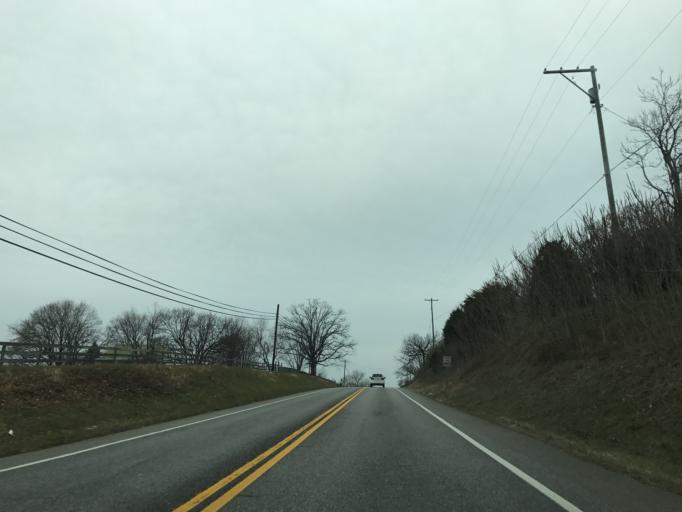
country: US
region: Maryland
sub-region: Frederick County
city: Emmitsburg
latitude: 39.7089
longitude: -77.3363
